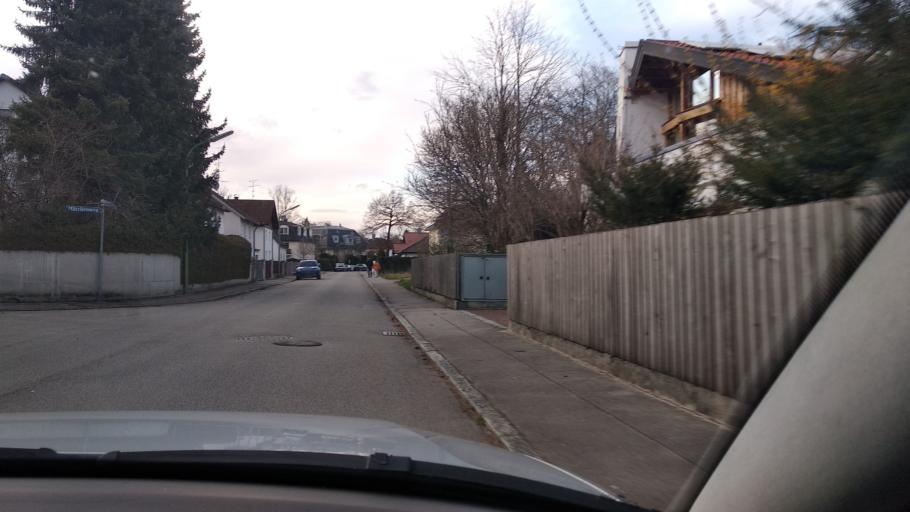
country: DE
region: Bavaria
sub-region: Upper Bavaria
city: Neubiberg
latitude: 48.0816
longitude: 11.6827
